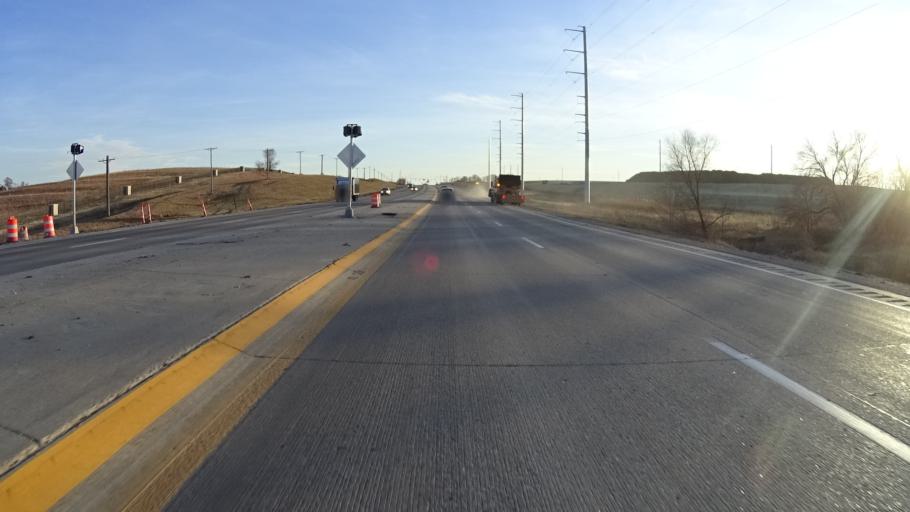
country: US
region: Nebraska
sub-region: Sarpy County
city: Chalco
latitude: 41.1382
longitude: -96.1392
